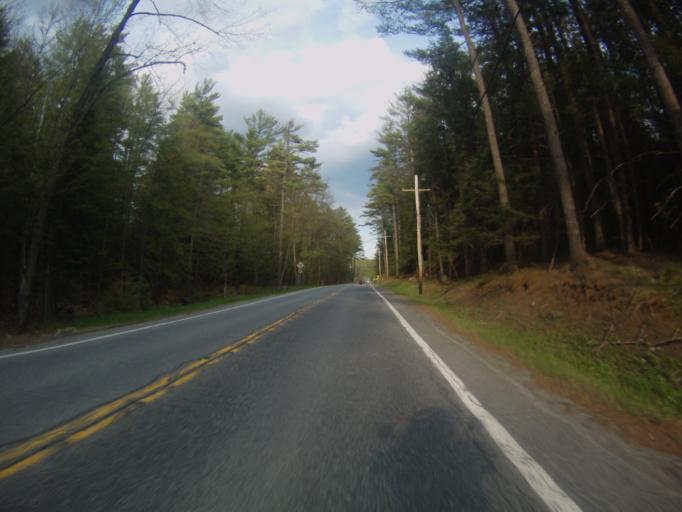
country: US
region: New York
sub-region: Warren County
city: Warrensburg
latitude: 43.6625
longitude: -73.8467
